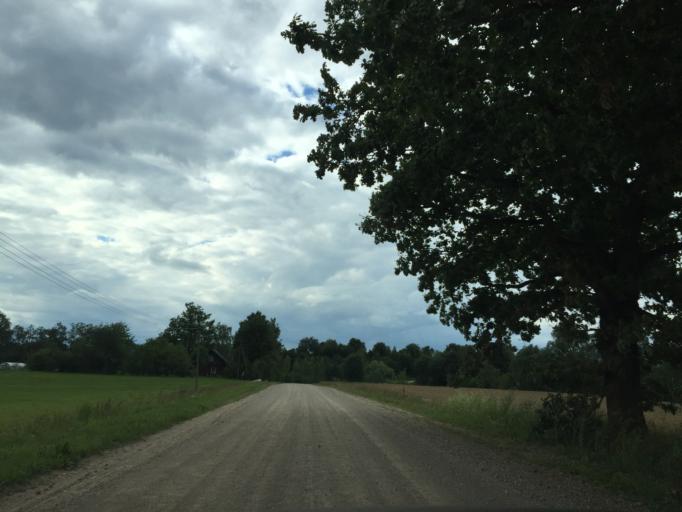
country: LV
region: Malpils
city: Malpils
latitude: 56.9573
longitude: 24.9873
